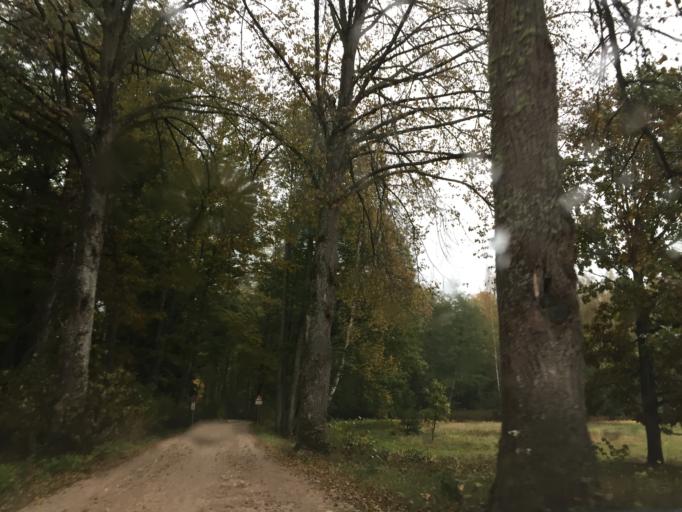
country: LV
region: Engure
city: Smarde
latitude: 56.9169
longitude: 23.4662
